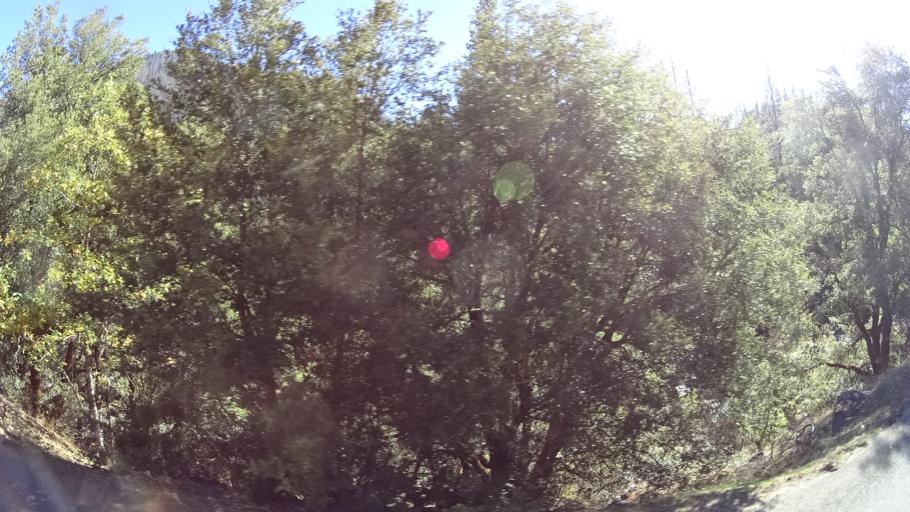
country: US
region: California
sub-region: Siskiyou County
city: Happy Camp
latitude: 41.2993
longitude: -123.0828
